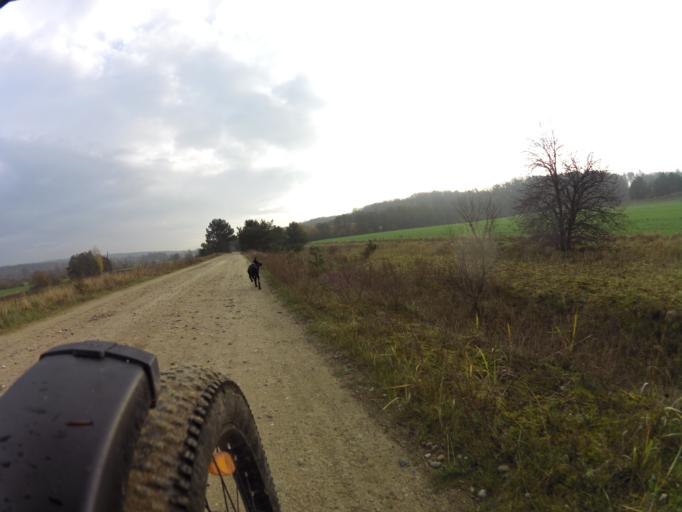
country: PL
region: Pomeranian Voivodeship
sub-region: Powiat wejherowski
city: Gniewino
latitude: 54.7064
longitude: 18.1025
